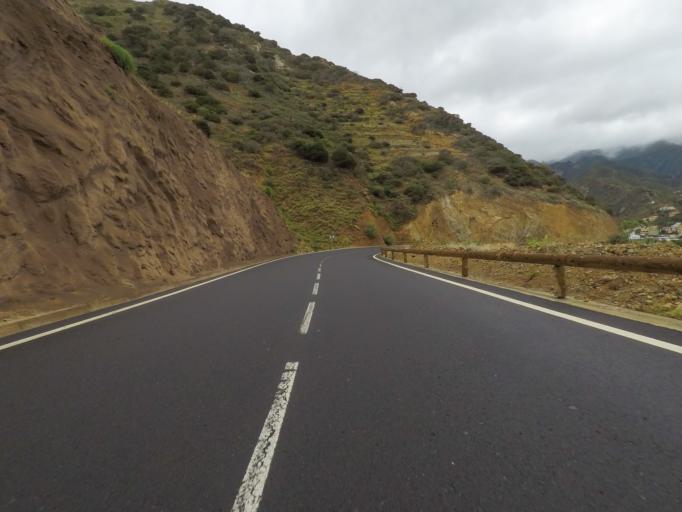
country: ES
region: Canary Islands
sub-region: Provincia de Santa Cruz de Tenerife
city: Vallehermosa
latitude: 28.1853
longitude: -17.2614
